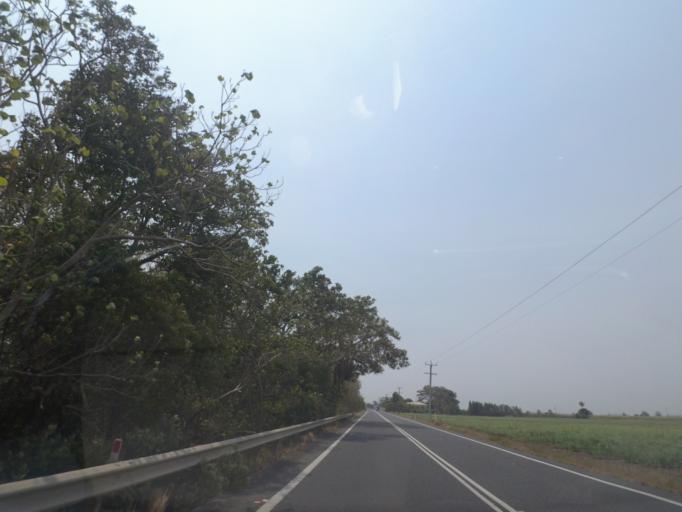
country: AU
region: New South Wales
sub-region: Richmond Valley
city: Evans Head
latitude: -28.9715
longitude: 153.4609
